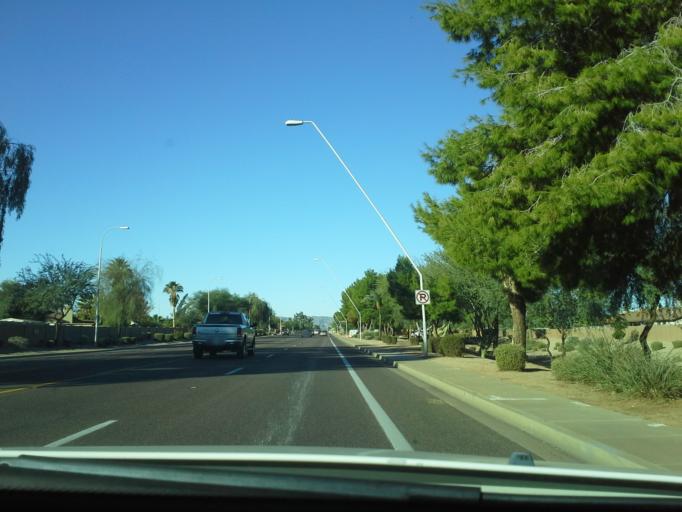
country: US
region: Arizona
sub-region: Maricopa County
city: San Carlos
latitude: 33.3497
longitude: -111.8637
